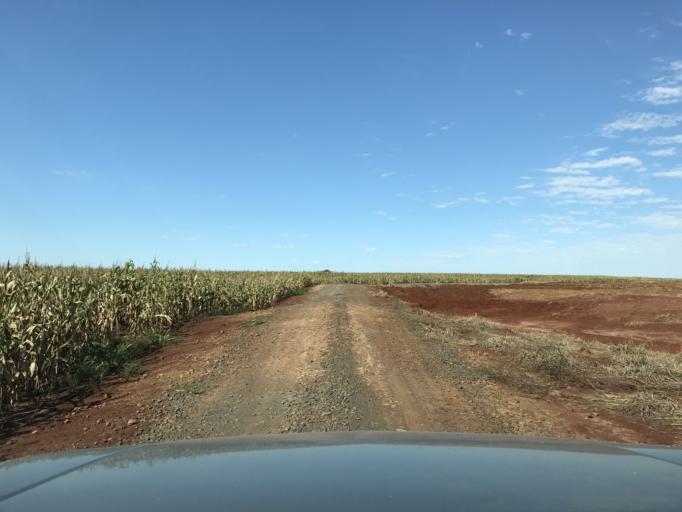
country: BR
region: Parana
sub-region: Ipora
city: Ipora
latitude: -24.1574
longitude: -53.7430
